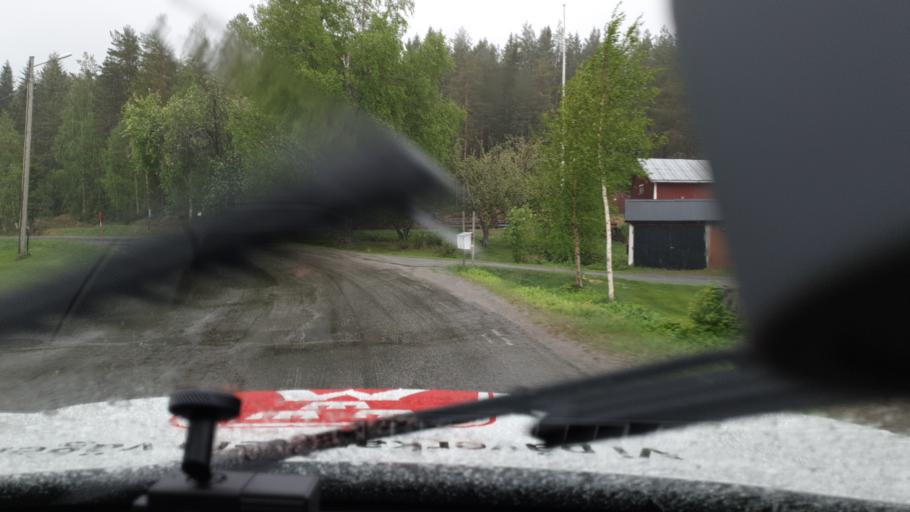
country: SE
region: Vaesterbotten
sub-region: Umea Kommun
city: Roback
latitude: 64.0288
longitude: 20.0841
